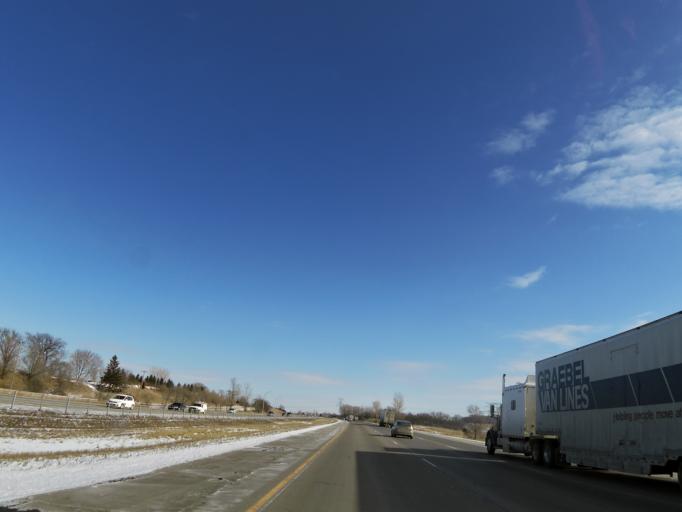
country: US
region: Minnesota
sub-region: Washington County
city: Afton
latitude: 44.9483
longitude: -92.8317
